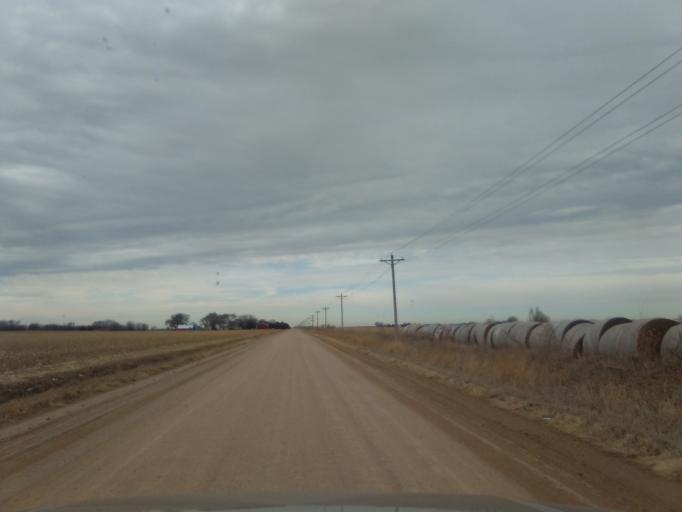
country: US
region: Nebraska
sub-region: Buffalo County
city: Gibbon
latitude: 40.6407
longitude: -98.8860
